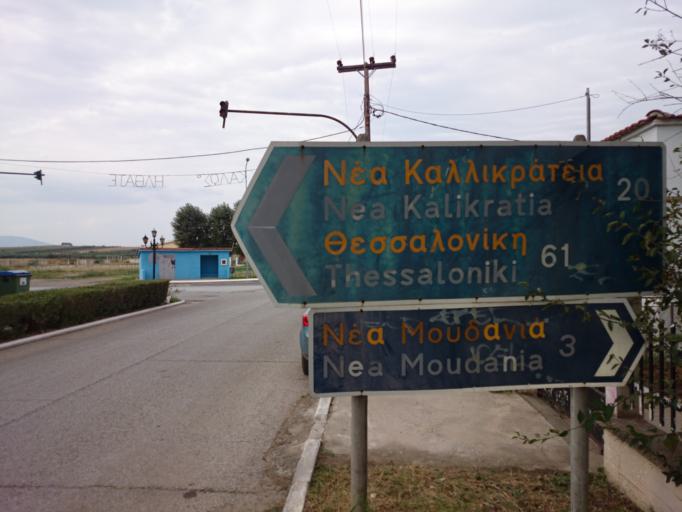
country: GR
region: Central Macedonia
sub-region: Nomos Chalkidikis
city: Nea Flogita
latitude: 40.2514
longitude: 23.2501
